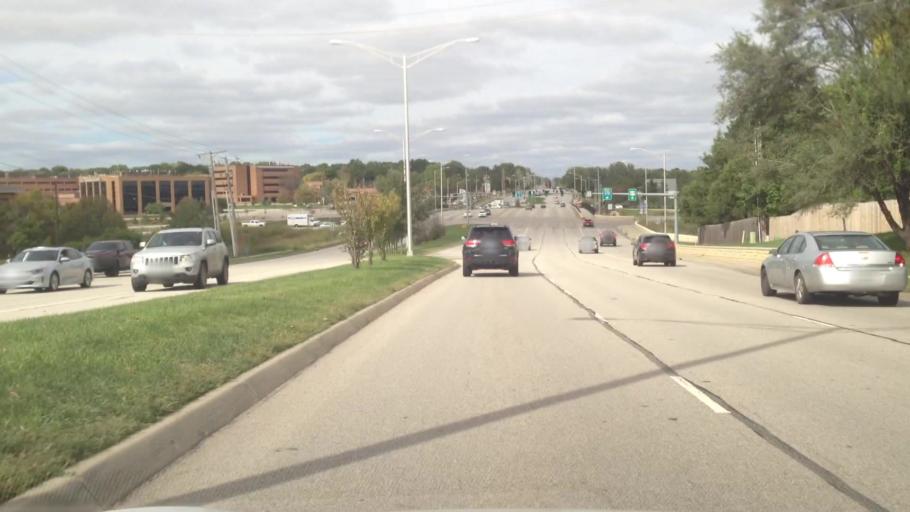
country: US
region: Kansas
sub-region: Johnson County
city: Lenexa
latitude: 38.9326
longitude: -94.7235
